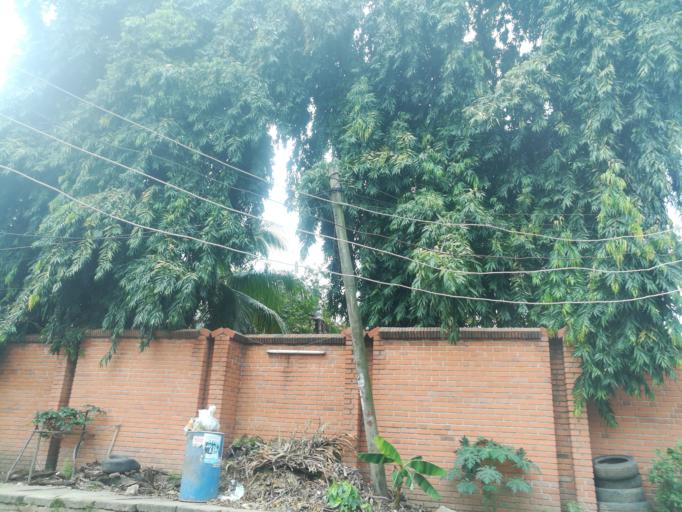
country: NG
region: Lagos
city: Ikeja
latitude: 6.5970
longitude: 3.3535
